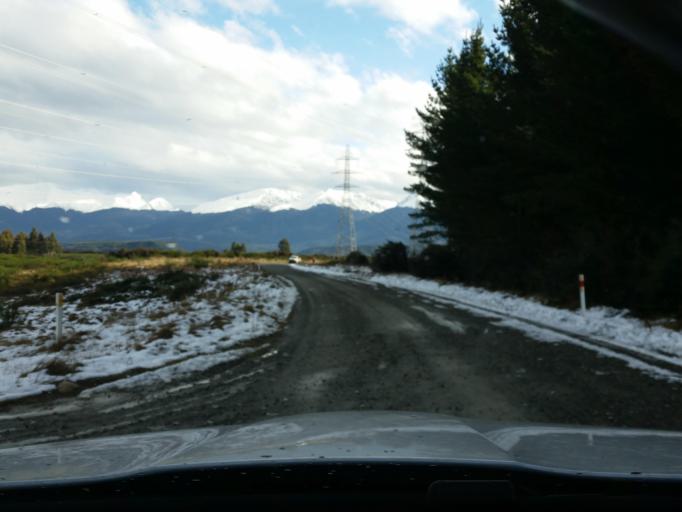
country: NZ
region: Southland
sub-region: Southland District
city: Te Anau
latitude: -45.7790
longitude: 167.5831
